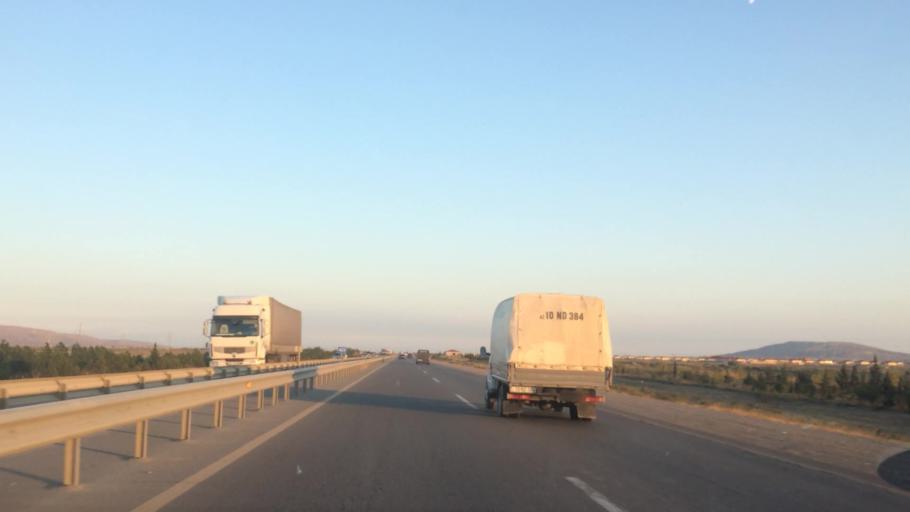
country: AZ
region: Baki
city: Qobustan
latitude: 39.9887
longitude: 49.2023
